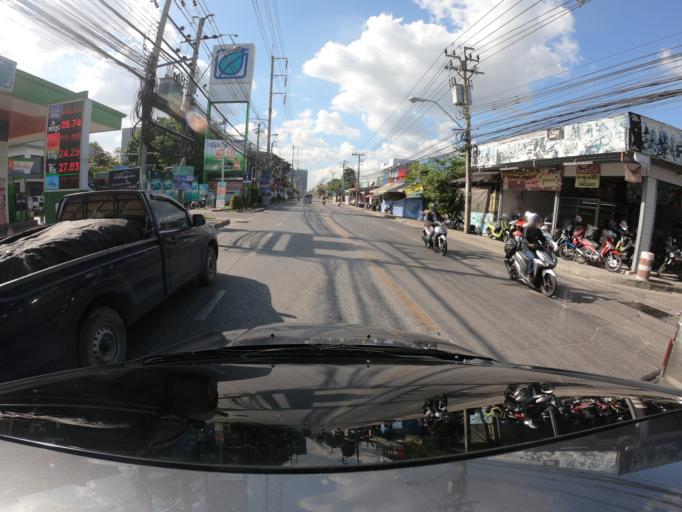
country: TH
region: Bangkok
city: Bang Na
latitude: 13.6545
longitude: 100.6117
